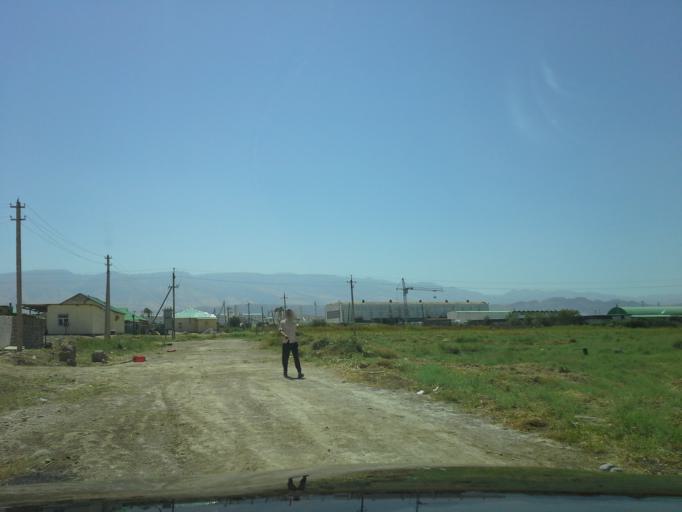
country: TM
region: Ahal
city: Ashgabat
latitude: 37.9997
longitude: 58.3181
